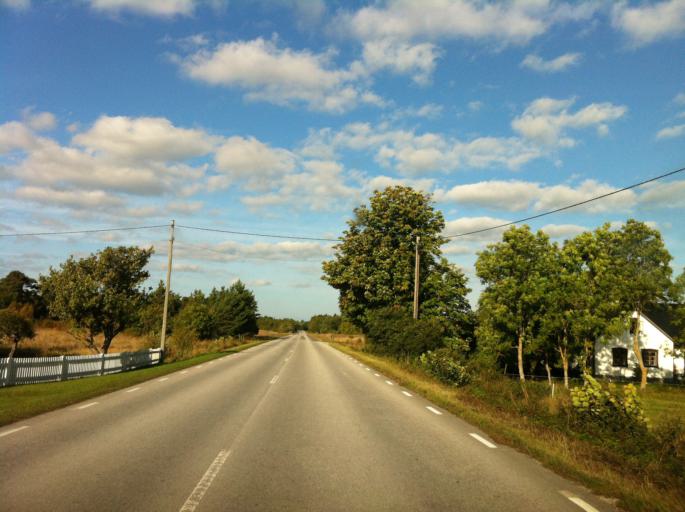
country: SE
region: Gotland
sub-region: Gotland
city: Slite
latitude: 57.4407
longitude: 18.7393
